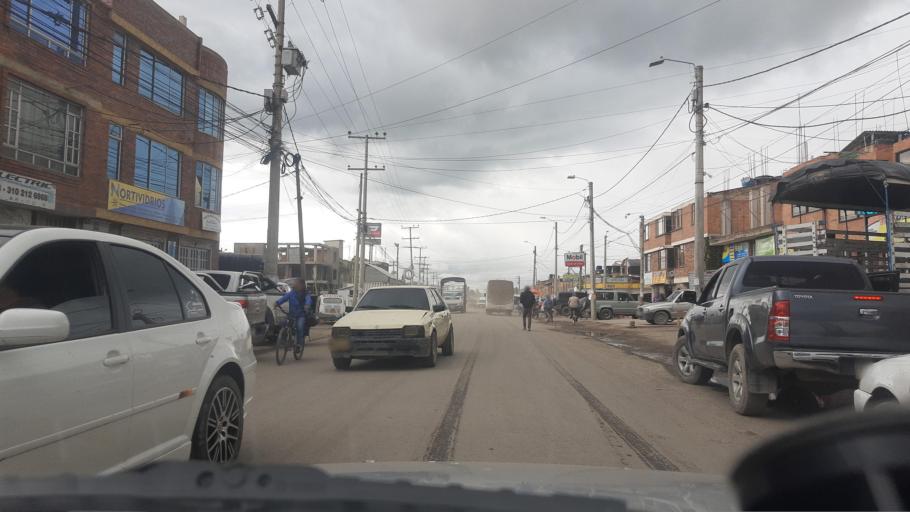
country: CO
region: Cundinamarca
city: Ubate
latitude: 5.3124
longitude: -73.8108
